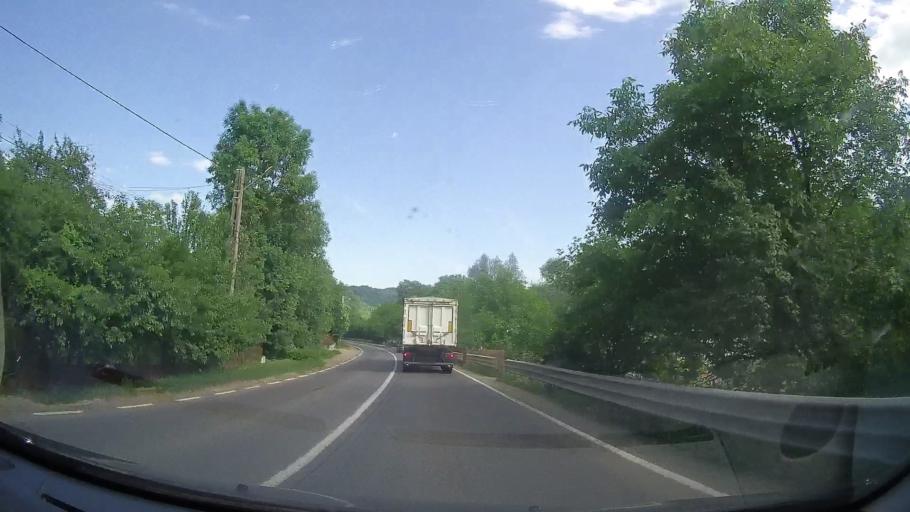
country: RO
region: Prahova
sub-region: Comuna Maneciu-Ungureni
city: Gheaba
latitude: 45.2883
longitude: 26.0005
